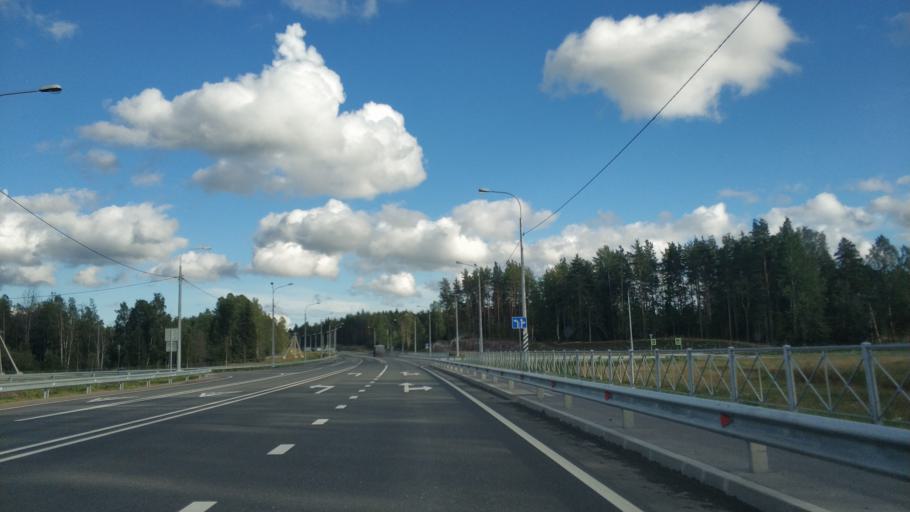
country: RU
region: Leningrad
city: Kuznechnoye
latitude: 61.0981
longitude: 29.9762
